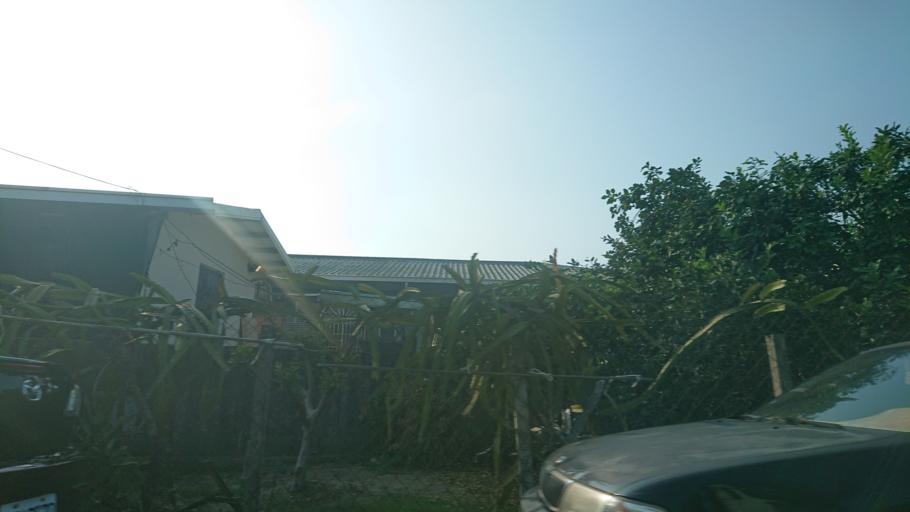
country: TW
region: Taiwan
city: Xinying
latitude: 23.1953
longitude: 120.2716
